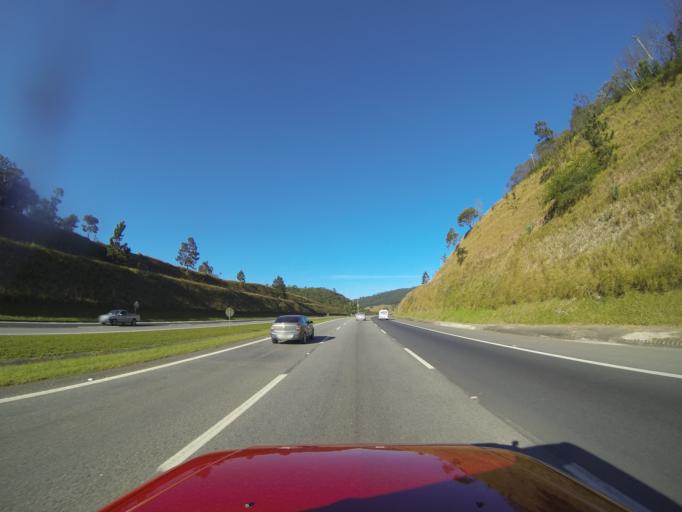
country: BR
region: Sao Paulo
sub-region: Piracaia
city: Piracaia
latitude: -23.1818
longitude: -46.3040
